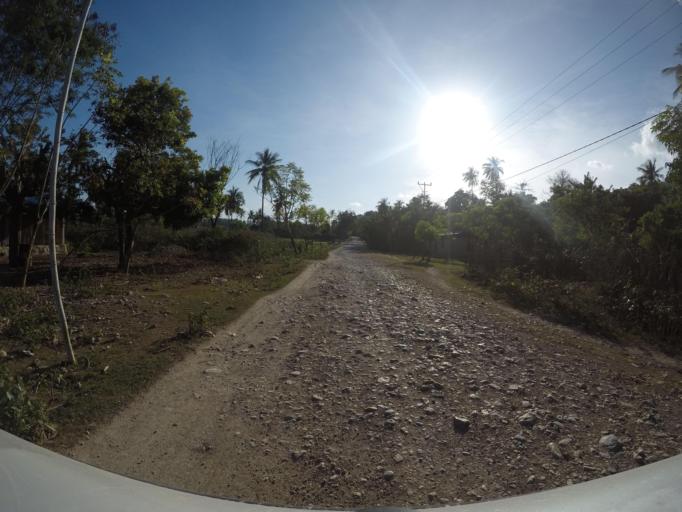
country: TL
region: Viqueque
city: Viqueque
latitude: -8.8043
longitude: 126.5795
